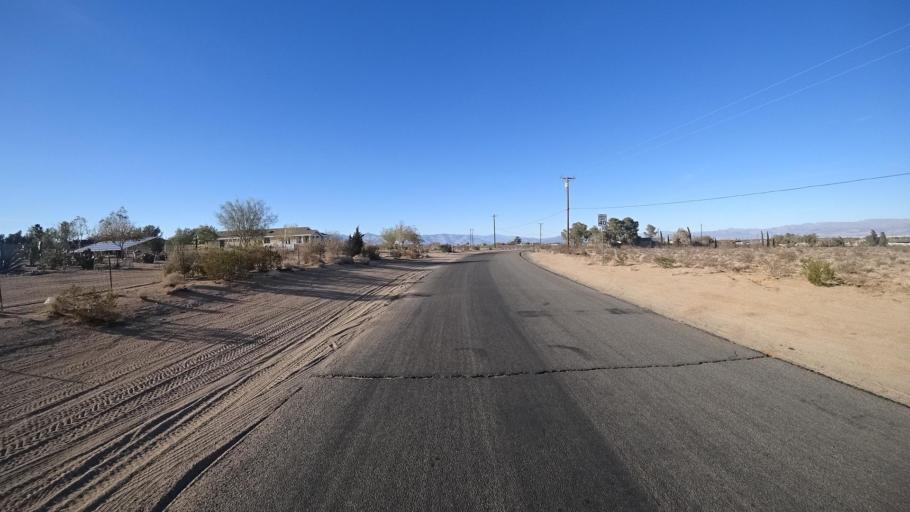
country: US
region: California
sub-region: Kern County
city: Ridgecrest
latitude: 35.5905
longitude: -117.6966
